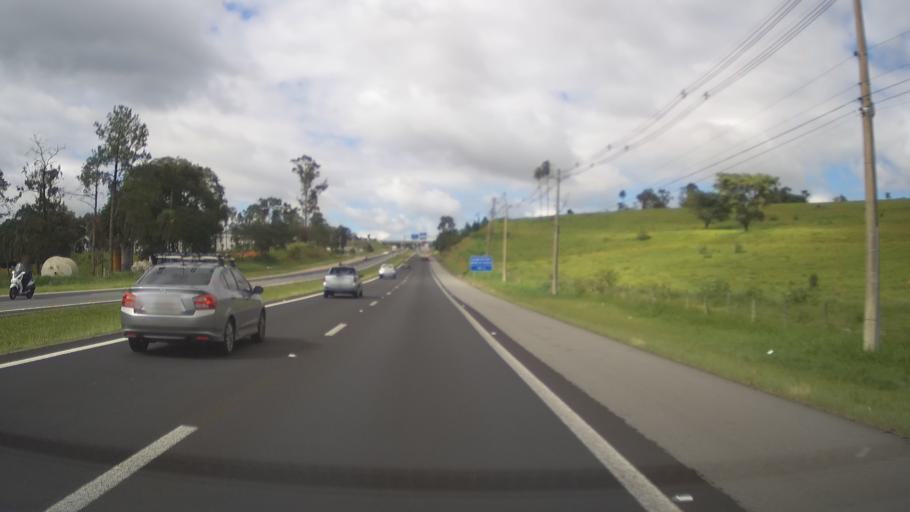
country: BR
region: Sao Paulo
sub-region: Itupeva
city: Itupeva
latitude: -23.2205
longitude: -47.0248
